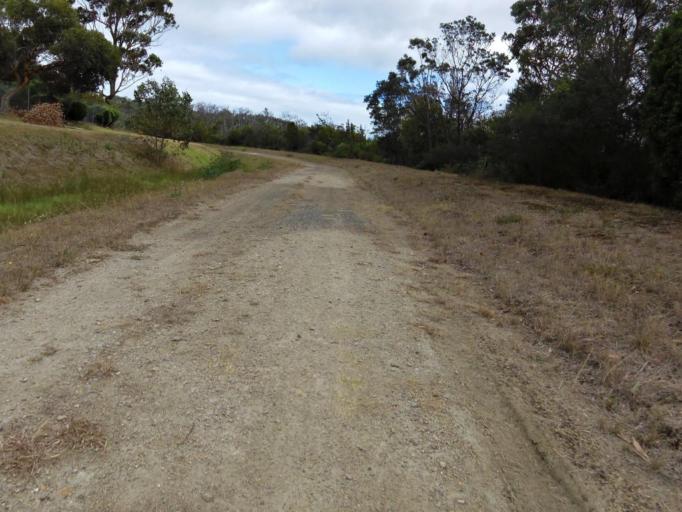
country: AU
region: Victoria
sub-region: Frankston
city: Frankston South
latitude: -38.1814
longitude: 145.1332
